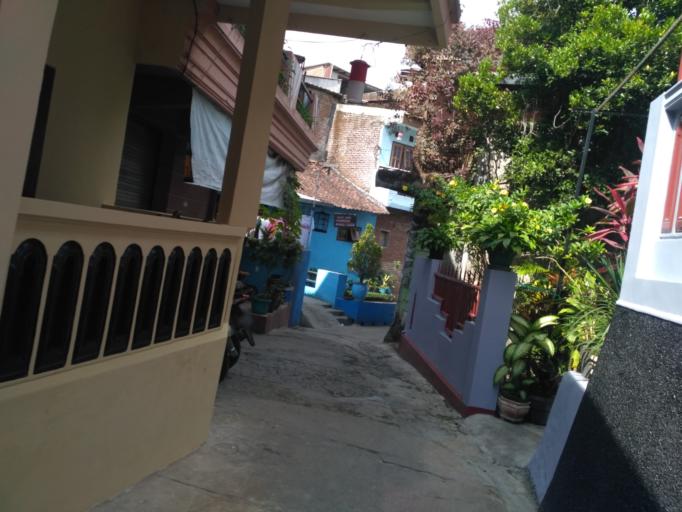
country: ID
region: East Java
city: Malang
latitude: -7.9371
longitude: 112.6049
